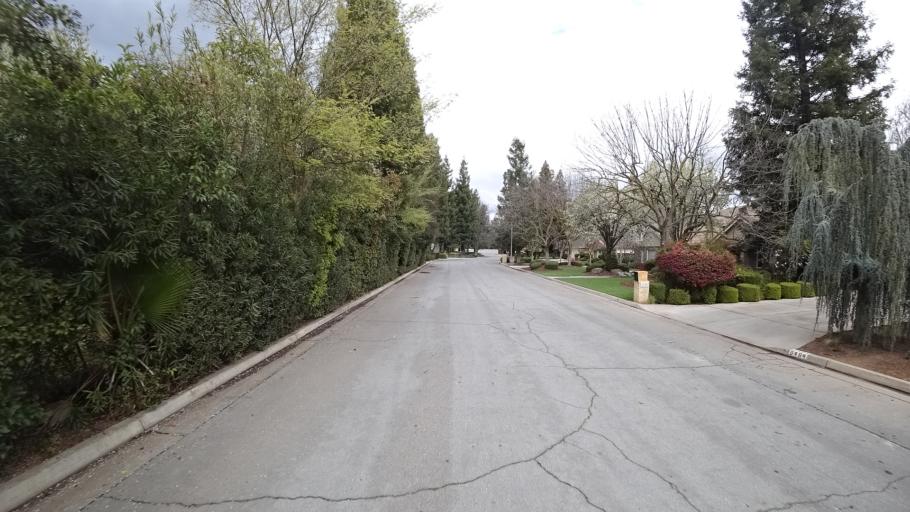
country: US
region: California
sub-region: Fresno County
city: Fresno
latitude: 36.8315
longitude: -119.8293
